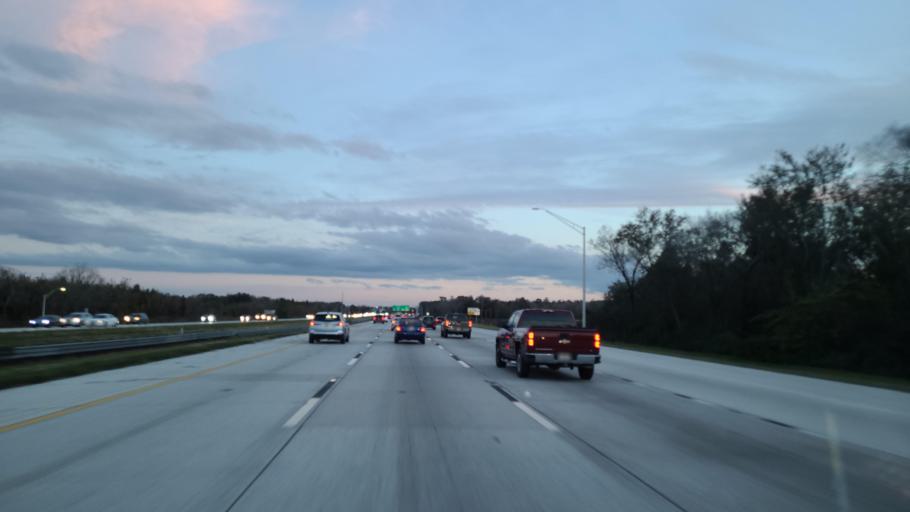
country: US
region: Florida
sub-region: Hillsborough County
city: Thonotosassa
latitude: 28.0257
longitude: -82.3354
